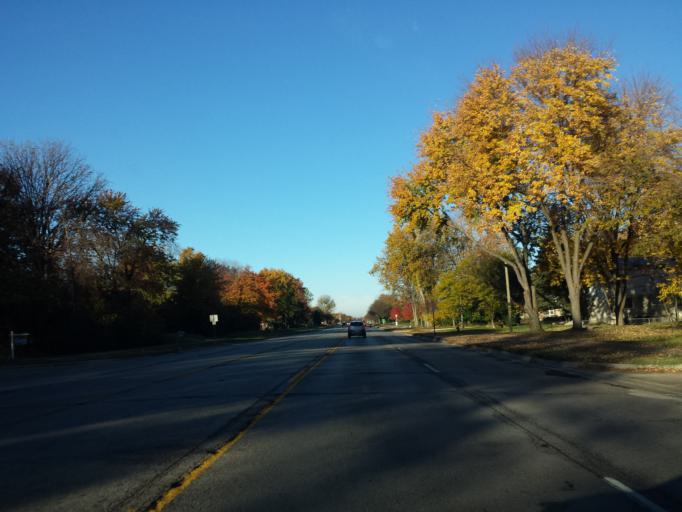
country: US
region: Michigan
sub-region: Oakland County
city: Bingham Farms
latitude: 42.5017
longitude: -83.2546
